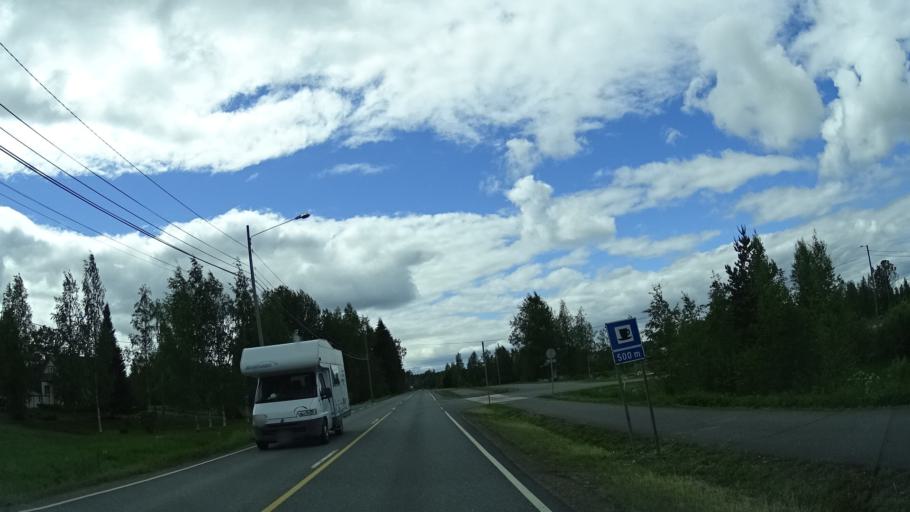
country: FI
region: Central Finland
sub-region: Joutsa
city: Luhanka
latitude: 61.8328
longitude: 25.8340
